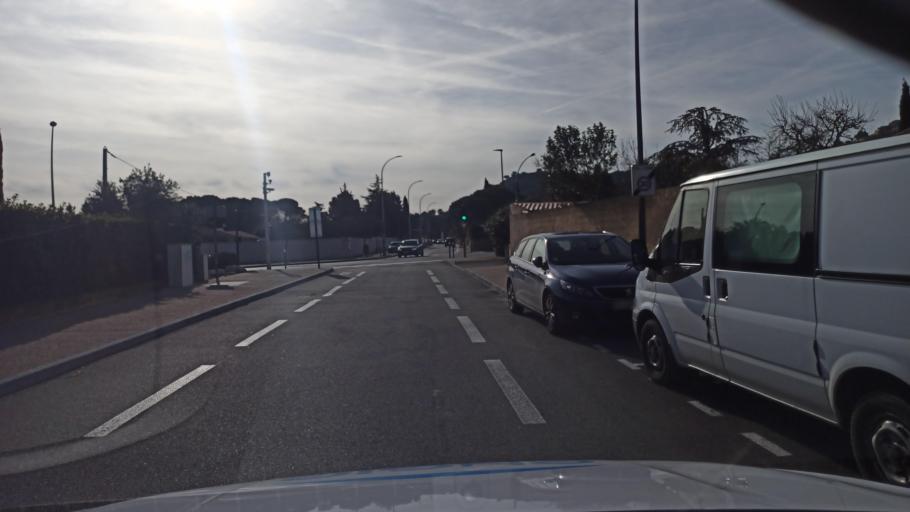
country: FR
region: Languedoc-Roussillon
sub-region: Departement du Gard
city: Villeneuve-les-Avignon
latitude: 43.9751
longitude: 4.7814
